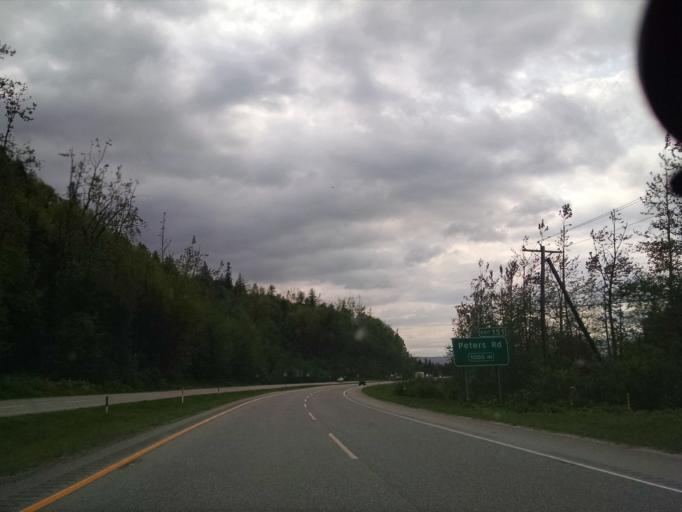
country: CA
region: British Columbia
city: Agassiz
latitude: 49.3023
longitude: -121.6448
